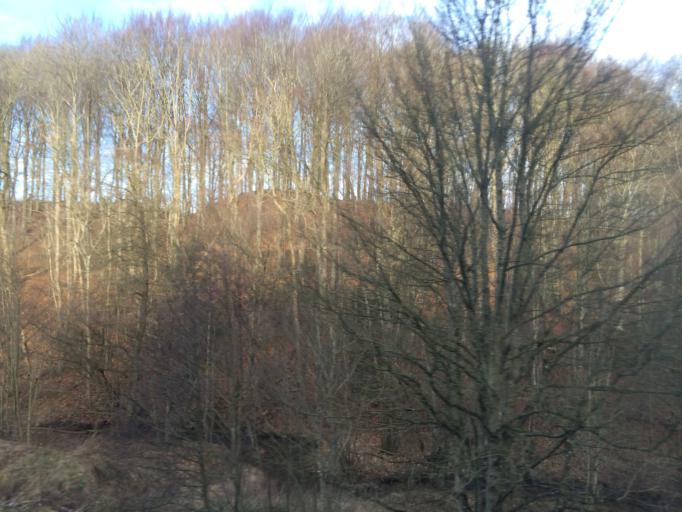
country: DK
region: South Denmark
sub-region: Vejle Kommune
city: Jelling
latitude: 55.7667
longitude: 9.4706
